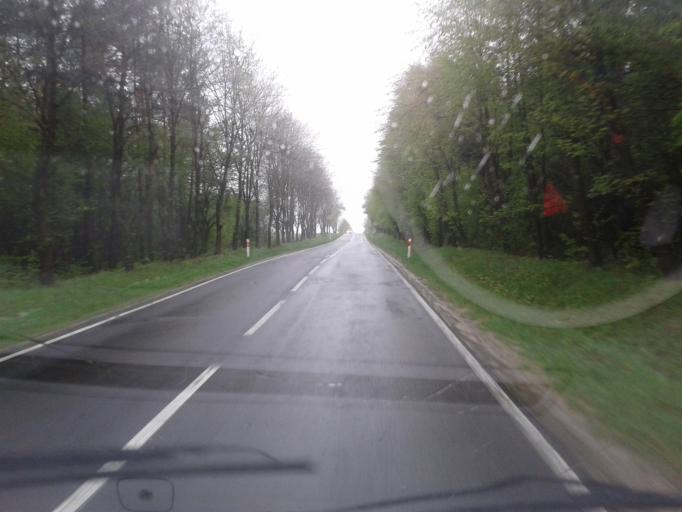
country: PL
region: Subcarpathian Voivodeship
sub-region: Powiat lubaczowski
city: Narol
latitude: 50.3264
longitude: 23.2796
